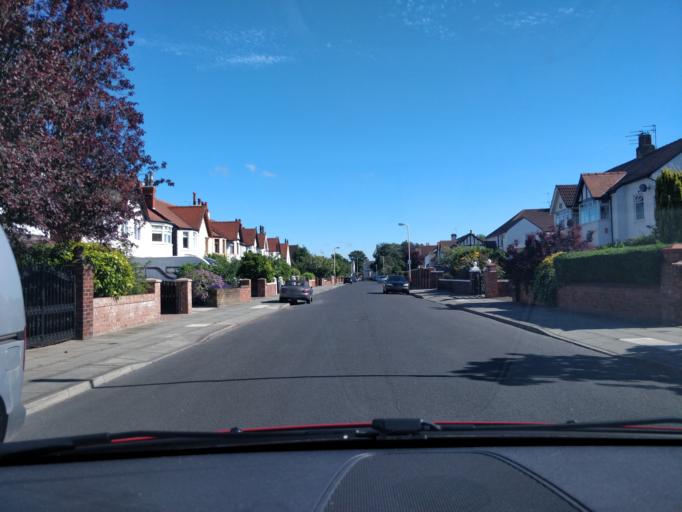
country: GB
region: England
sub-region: Sefton
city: Southport
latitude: 53.6561
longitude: -2.9676
